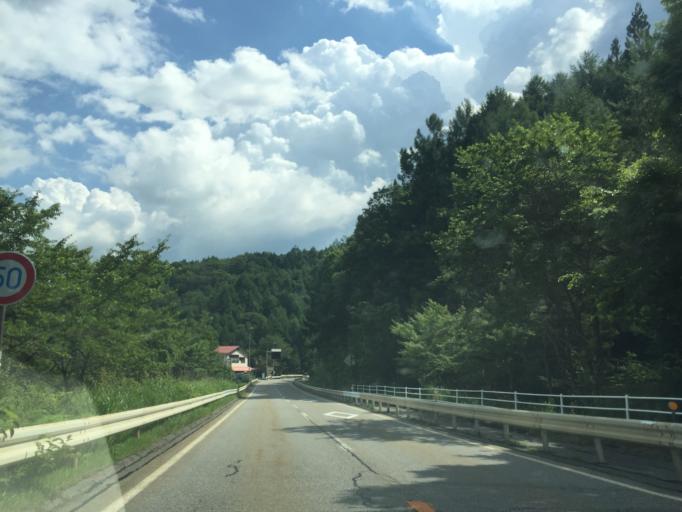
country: JP
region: Nagano
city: Iida
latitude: 35.3808
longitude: 137.6839
